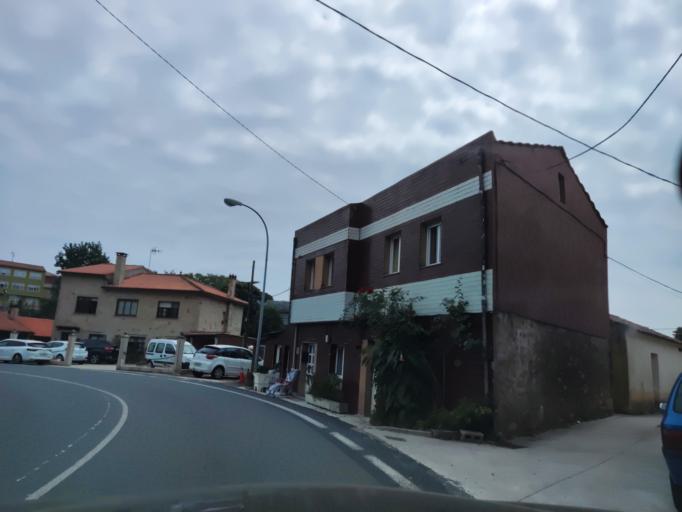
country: ES
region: Galicia
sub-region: Provincia da Coruna
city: Boiro
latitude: 42.6461
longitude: -8.8939
